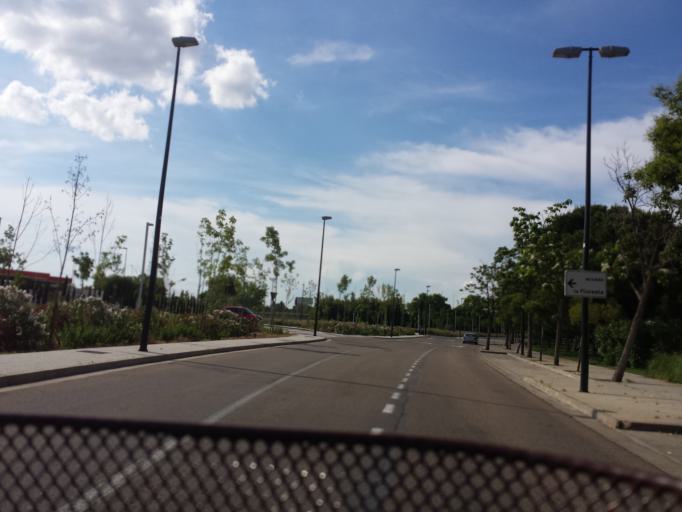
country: ES
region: Aragon
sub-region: Provincia de Zaragoza
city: Oliver-Valdefierro, Oliver, Valdefierro
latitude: 41.6337
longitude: -0.9219
